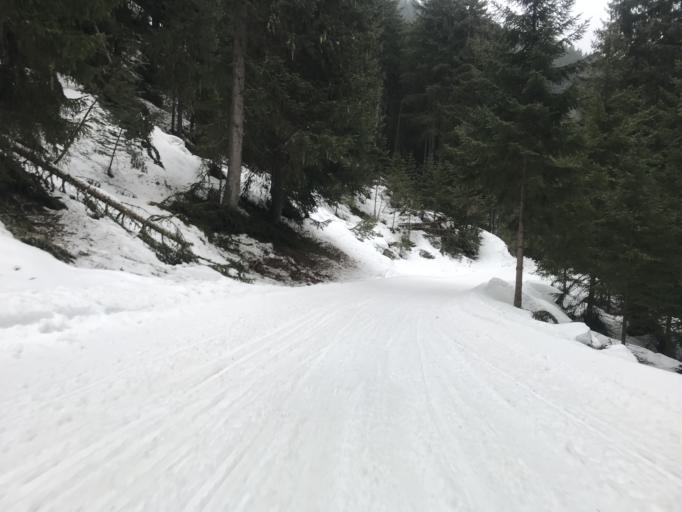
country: IT
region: Trentino-Alto Adige
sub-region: Bolzano
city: Funes - Villnoess
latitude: 46.6837
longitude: 11.6906
